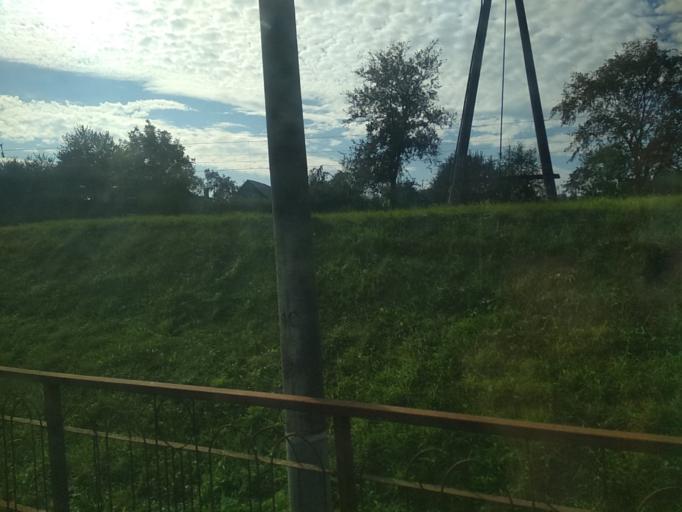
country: BY
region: Minsk
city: Syenitsa
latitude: 53.8177
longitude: 27.5736
